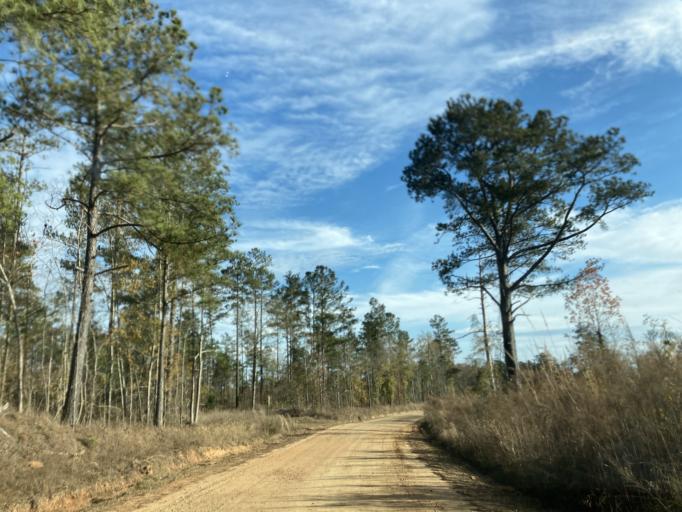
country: US
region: Georgia
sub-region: Jones County
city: Gray
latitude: 32.8948
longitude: -83.4898
